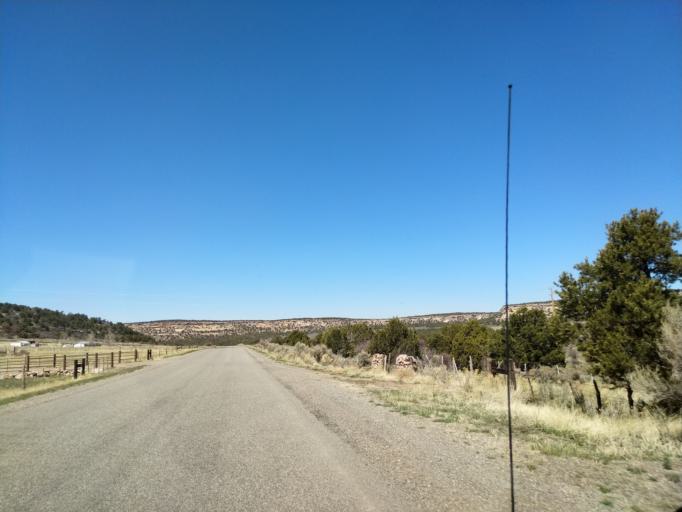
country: US
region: Colorado
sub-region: Mesa County
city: Loma
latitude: 38.9570
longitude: -109.0013
